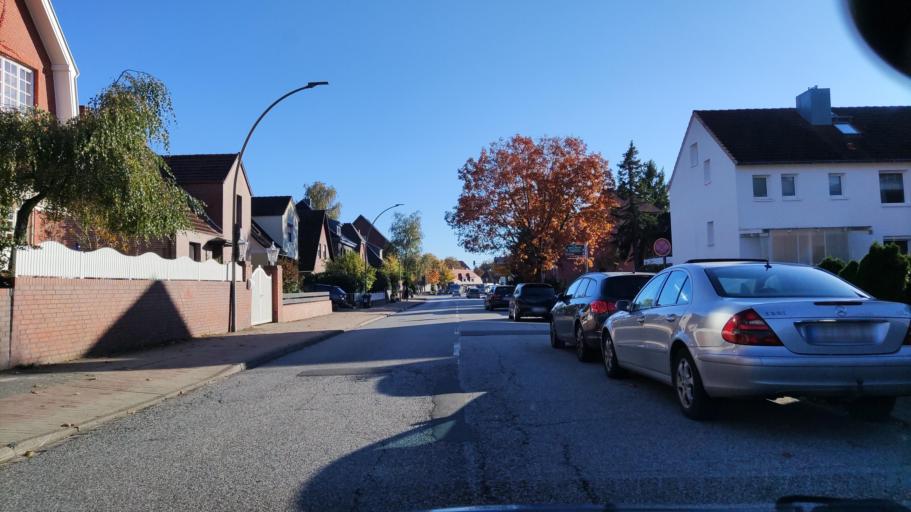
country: DE
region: Schleswig-Holstein
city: Geesthacht
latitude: 53.4380
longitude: 10.3730
